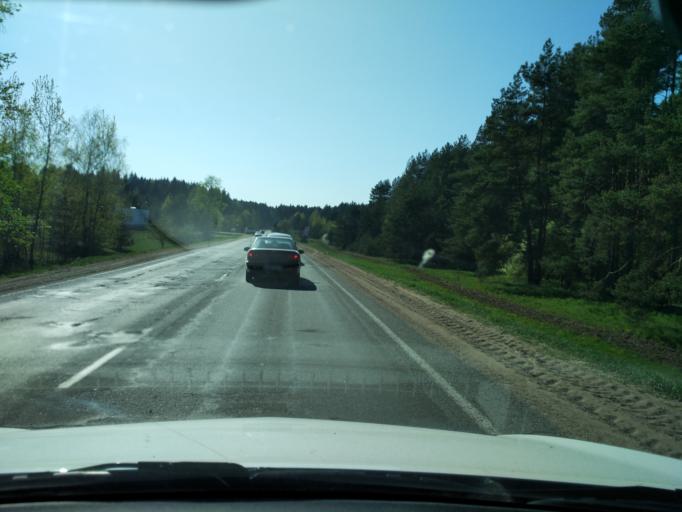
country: BY
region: Minsk
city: Lyeskawka
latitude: 53.9611
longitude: 27.7053
